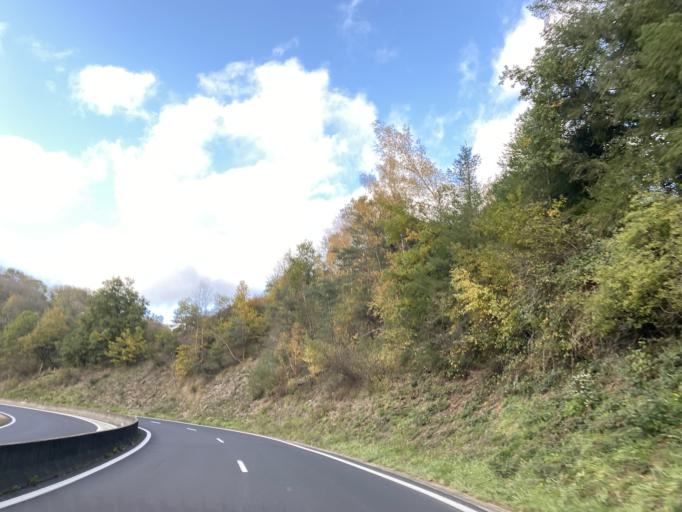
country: FR
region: Auvergne
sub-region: Departement du Puy-de-Dome
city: Courpiere
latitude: 45.7099
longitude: 3.5903
